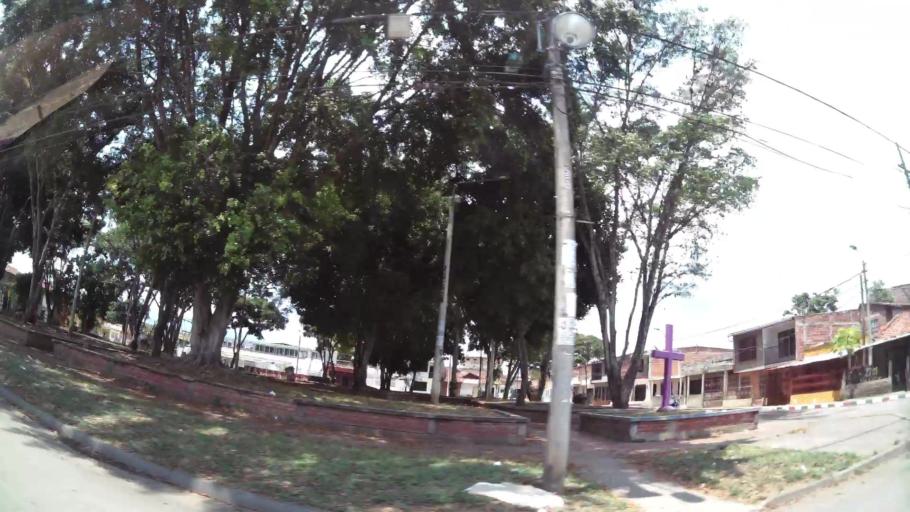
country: CO
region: Valle del Cauca
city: Cali
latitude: 3.4488
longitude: -76.4790
